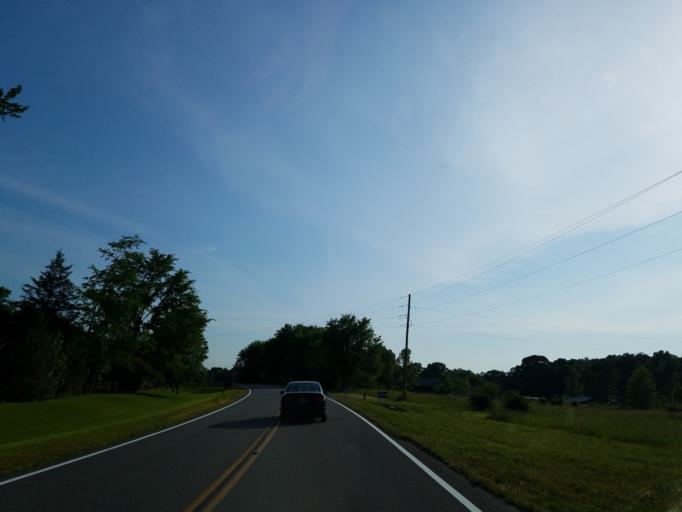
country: US
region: Georgia
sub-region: Chattooga County
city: Trion
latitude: 34.5507
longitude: -85.1972
